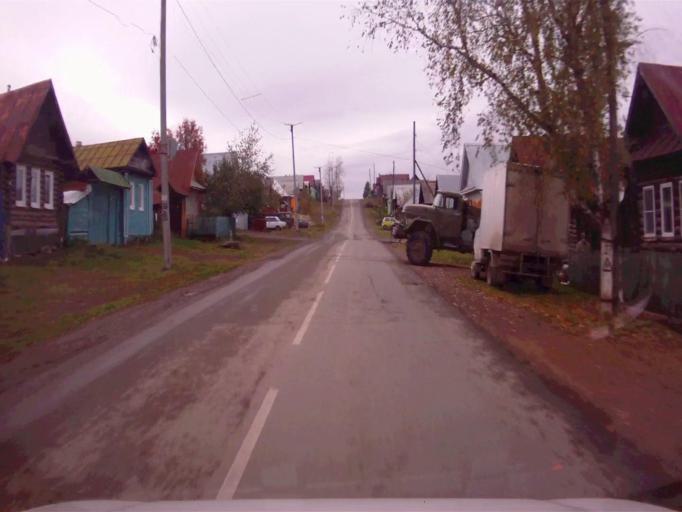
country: RU
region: Chelyabinsk
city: Nyazepetrovsk
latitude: 56.0609
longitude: 59.5783
